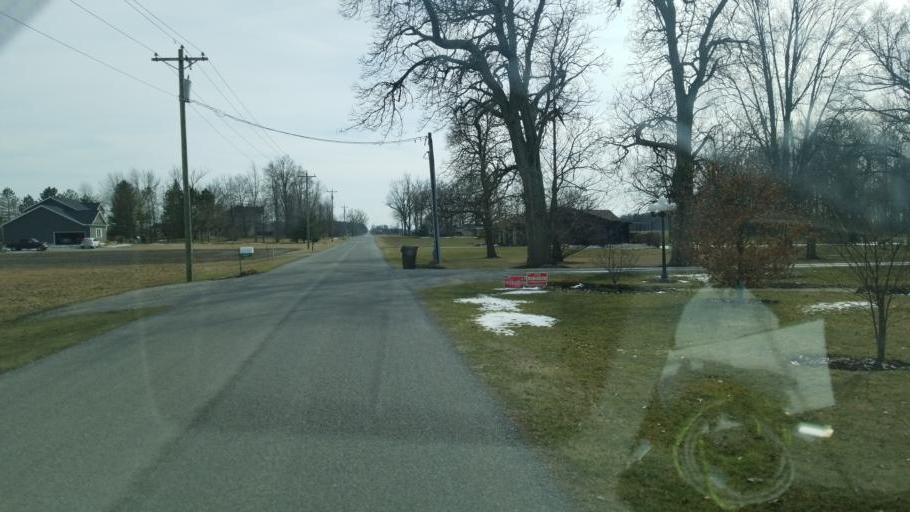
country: US
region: Ohio
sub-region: Union County
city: Marysville
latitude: 40.3097
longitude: -83.2749
